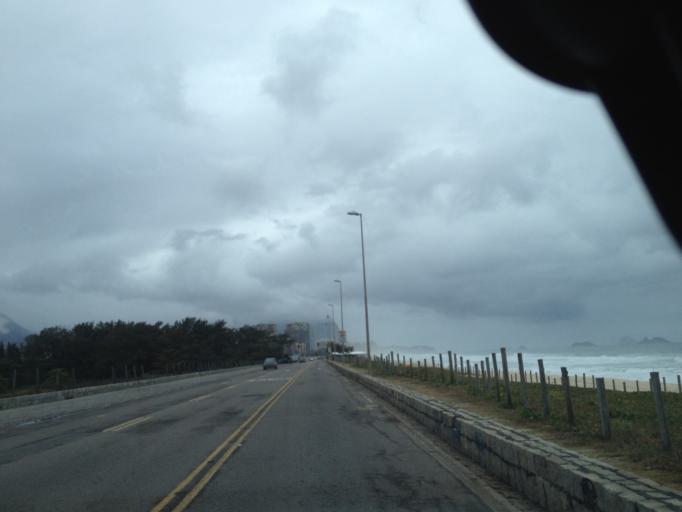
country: BR
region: Rio de Janeiro
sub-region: Rio De Janeiro
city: Rio de Janeiro
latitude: -23.0118
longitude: -43.3796
